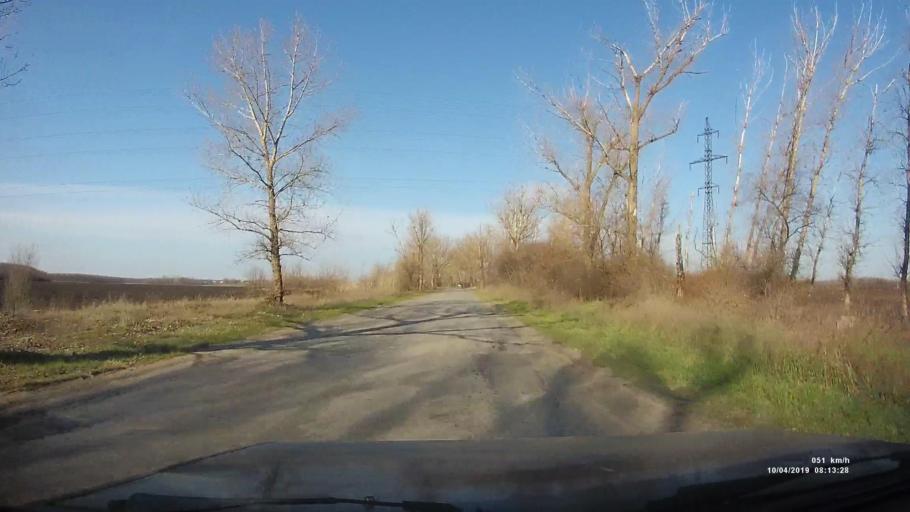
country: RU
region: Rostov
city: Masalovka
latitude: 48.3614
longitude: 40.2462
